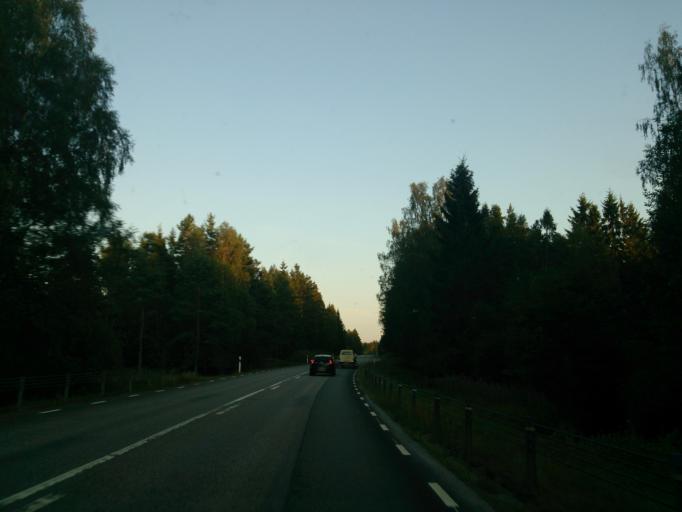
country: SE
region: Joenkoeping
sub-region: Varnamo Kommun
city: Rydaholm
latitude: 56.9215
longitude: 14.4194
